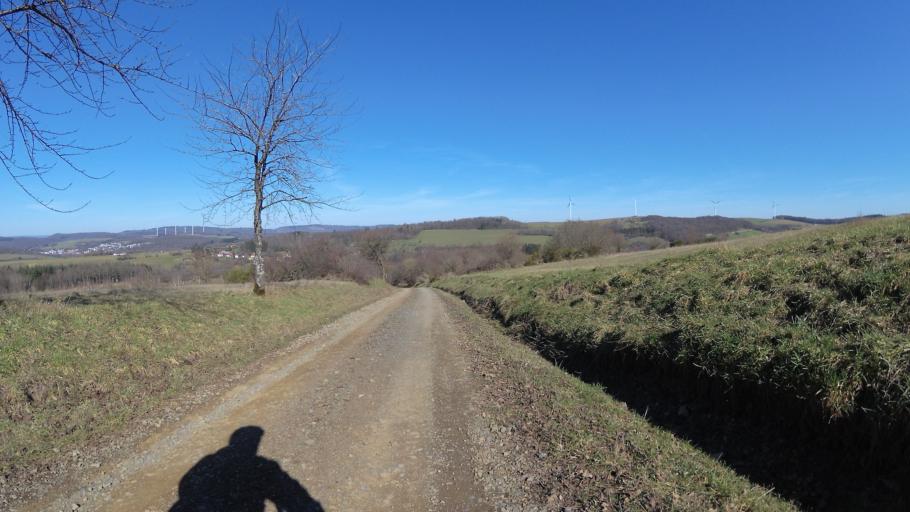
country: DE
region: Rheinland-Pfalz
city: Breitenbach
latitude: 49.4613
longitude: 7.2682
